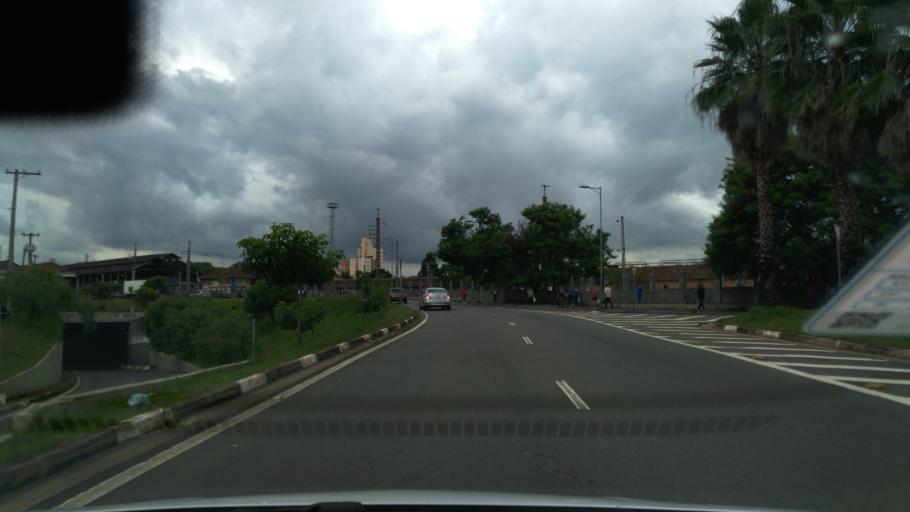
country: BR
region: Sao Paulo
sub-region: Campinas
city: Campinas
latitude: -22.9074
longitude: -47.0697
